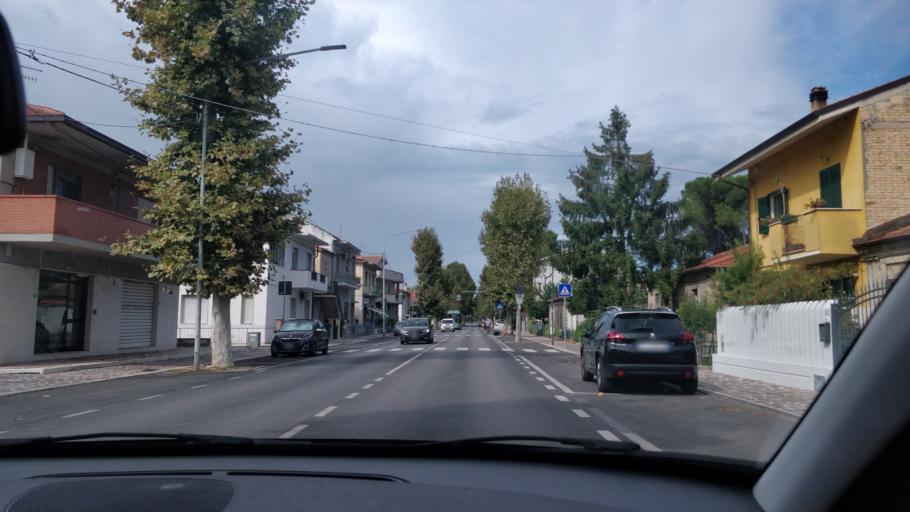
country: IT
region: Abruzzo
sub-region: Provincia di Chieti
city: Sambuceto
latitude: 42.4218
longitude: 14.1828
